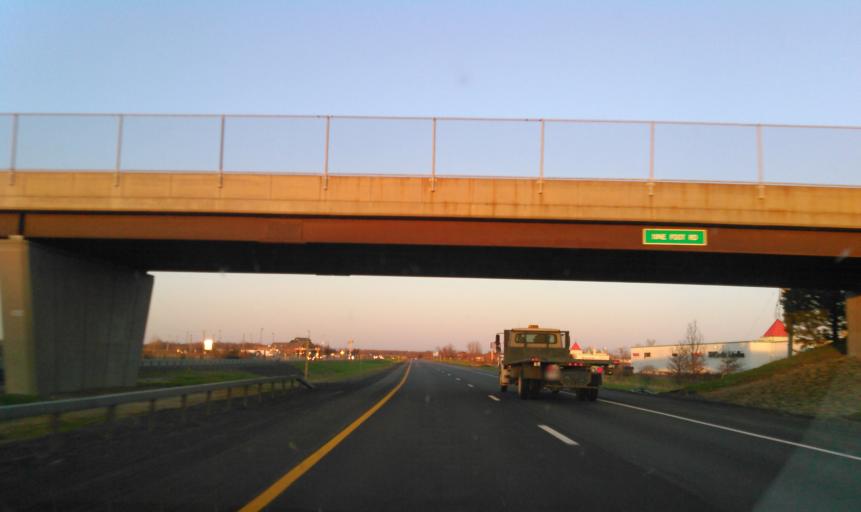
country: US
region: New York
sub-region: Seneca County
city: Waterloo
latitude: 42.9579
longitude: -76.9252
